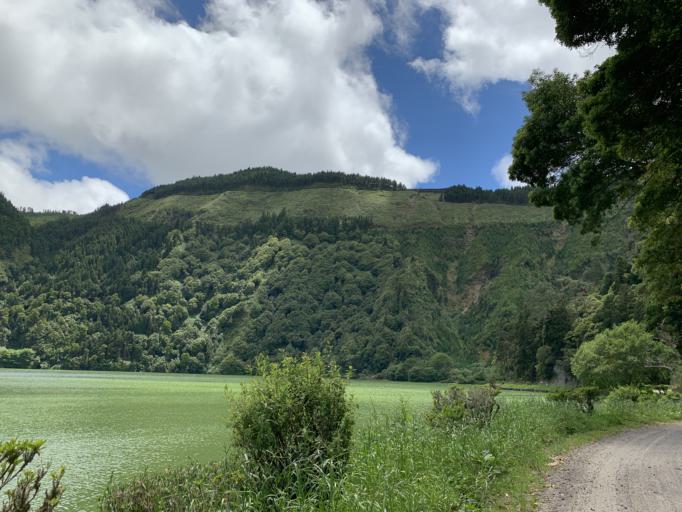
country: PT
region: Azores
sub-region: Ponta Delgada
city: Arrifes
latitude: 37.8467
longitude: -25.7935
